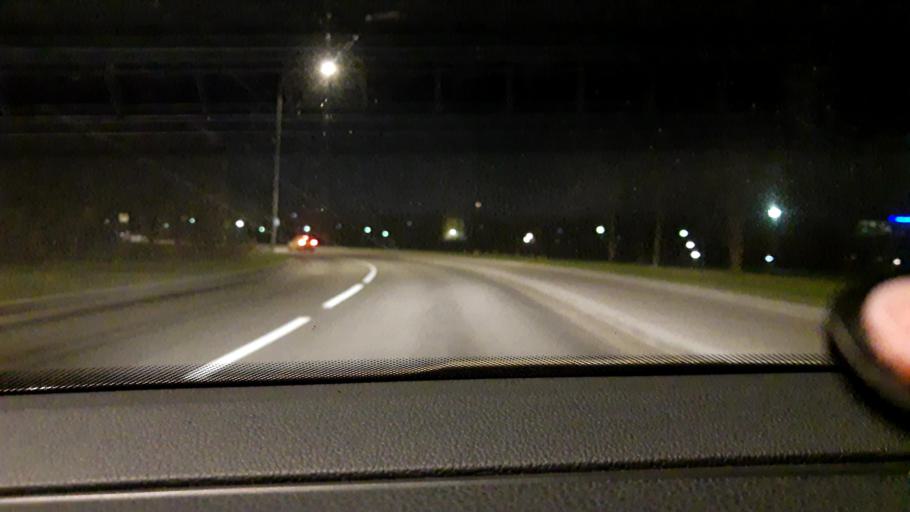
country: RU
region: Moscow
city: Brateyevo
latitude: 55.6301
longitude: 37.7591
